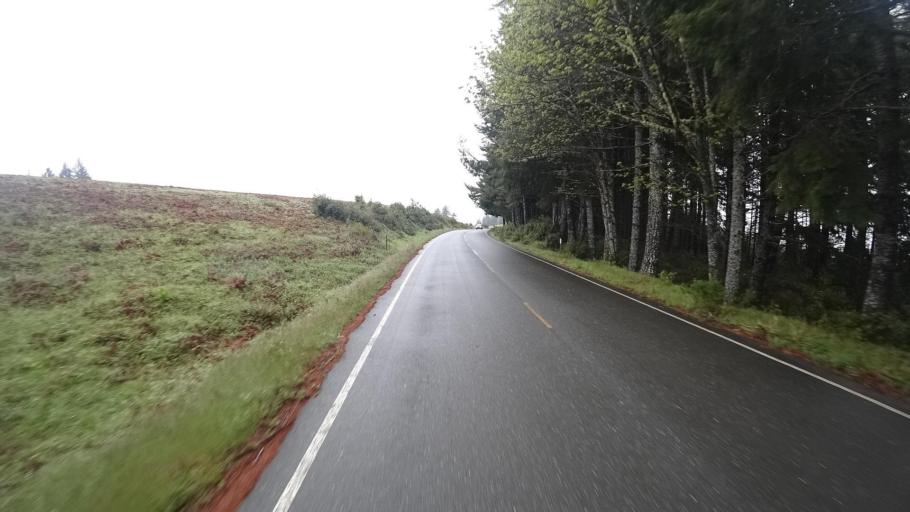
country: US
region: California
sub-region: Humboldt County
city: Westhaven-Moonstone
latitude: 41.1910
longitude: -123.9355
